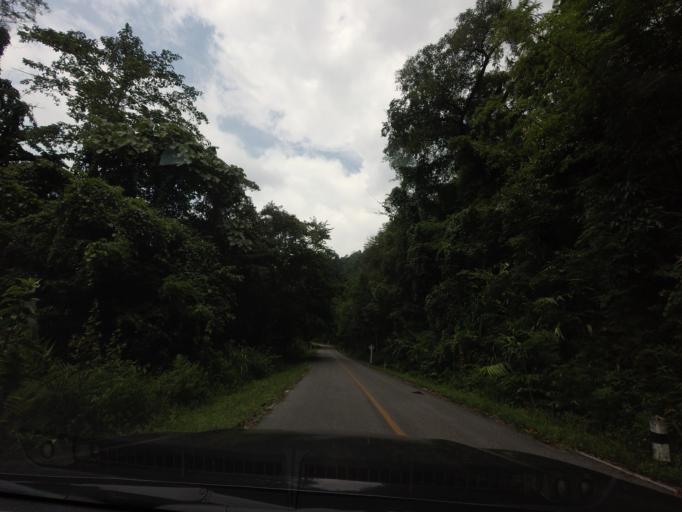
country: TH
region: Loei
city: Na Haeo
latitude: 17.7102
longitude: 100.9473
